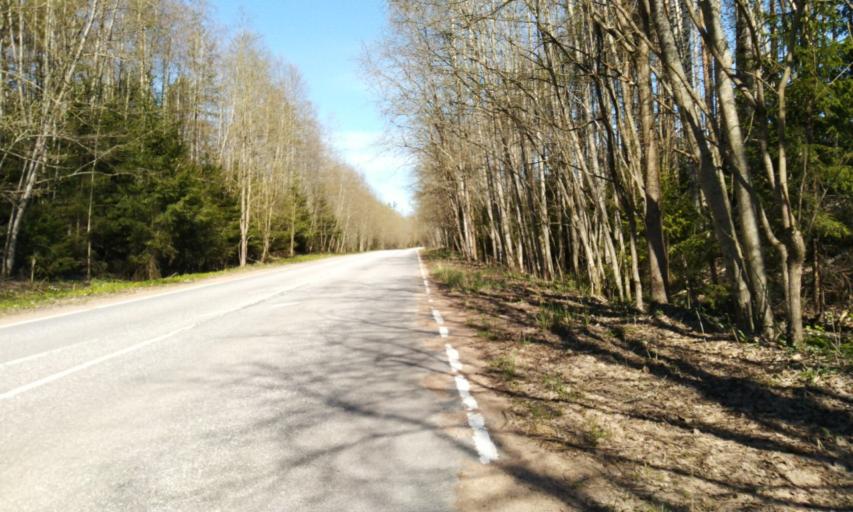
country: RU
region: Leningrad
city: Garbolovo
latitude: 60.4069
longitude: 30.4652
